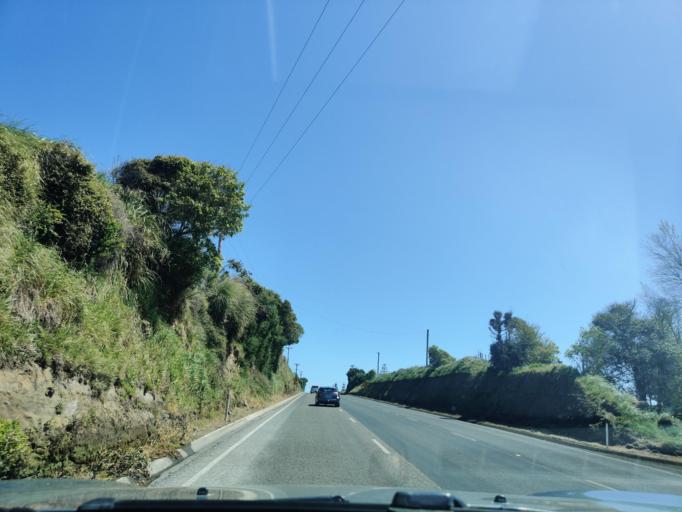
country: NZ
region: Taranaki
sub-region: South Taranaki District
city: Hawera
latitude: -39.6160
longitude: 174.3372
